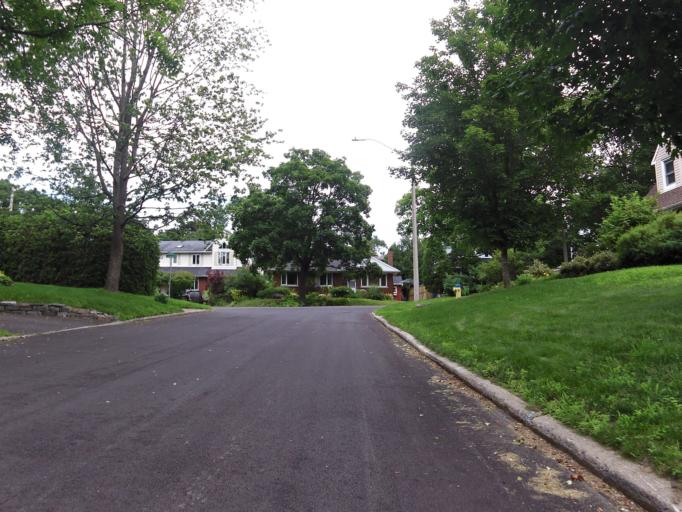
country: CA
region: Ontario
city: Ottawa
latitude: 45.3893
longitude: -75.6671
